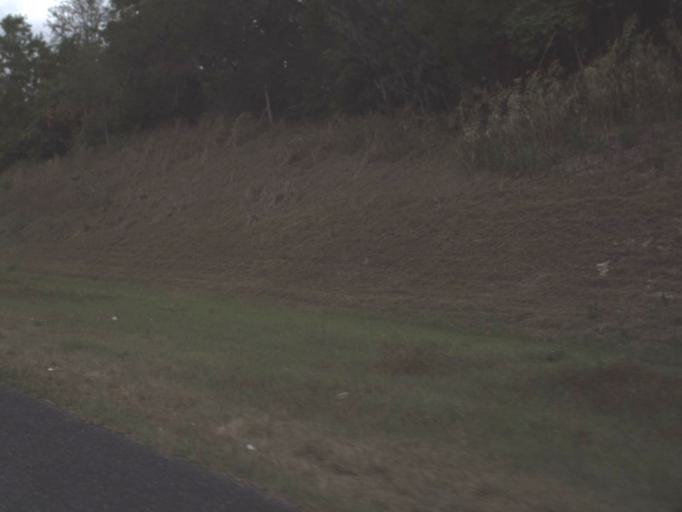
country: US
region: Florida
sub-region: Marion County
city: Ocala
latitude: 29.2608
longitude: -82.1663
